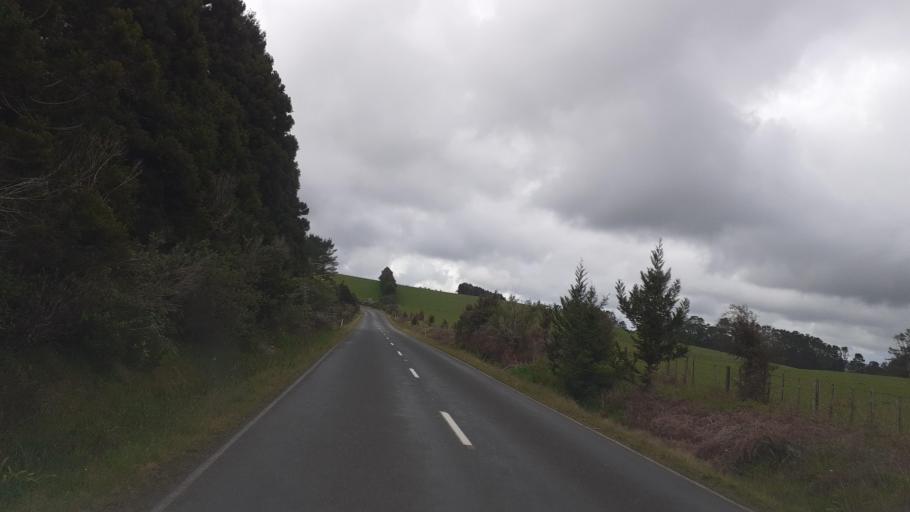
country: NZ
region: Northland
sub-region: Far North District
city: Waimate North
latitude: -35.2623
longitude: 173.8099
